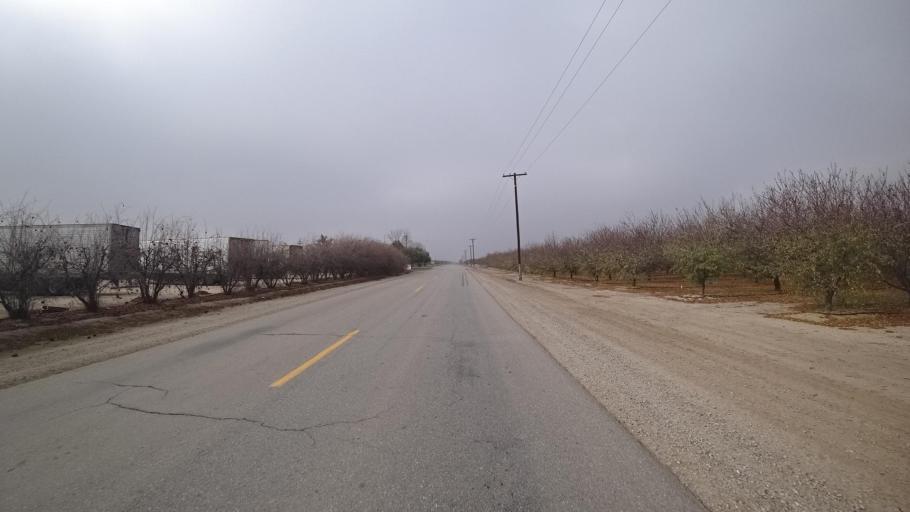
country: US
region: California
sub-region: Kern County
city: Maricopa
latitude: 35.0940
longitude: -119.2088
